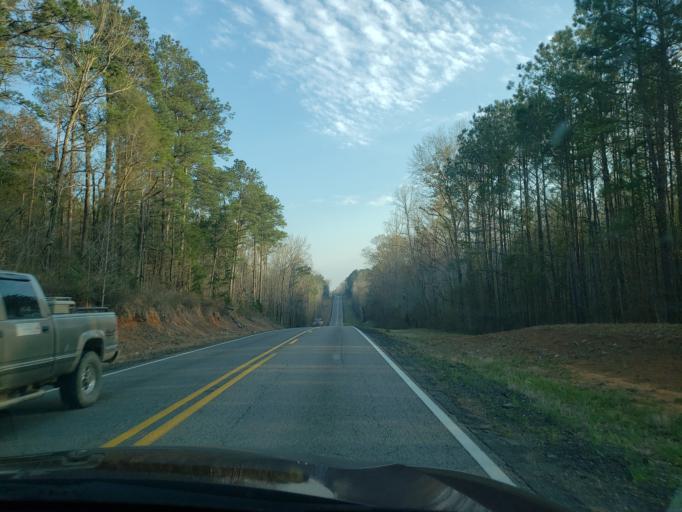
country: US
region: Alabama
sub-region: Hale County
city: Greensboro
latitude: 32.7905
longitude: -87.5903
